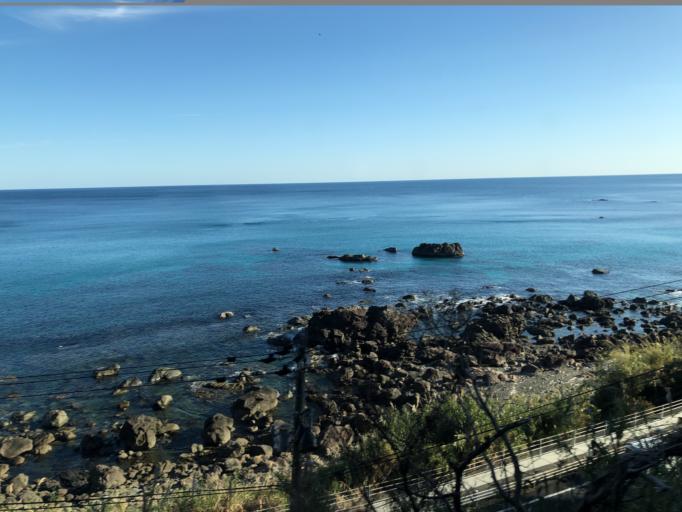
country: JP
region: Kochi
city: Nakamura
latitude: 33.0602
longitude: 133.1005
